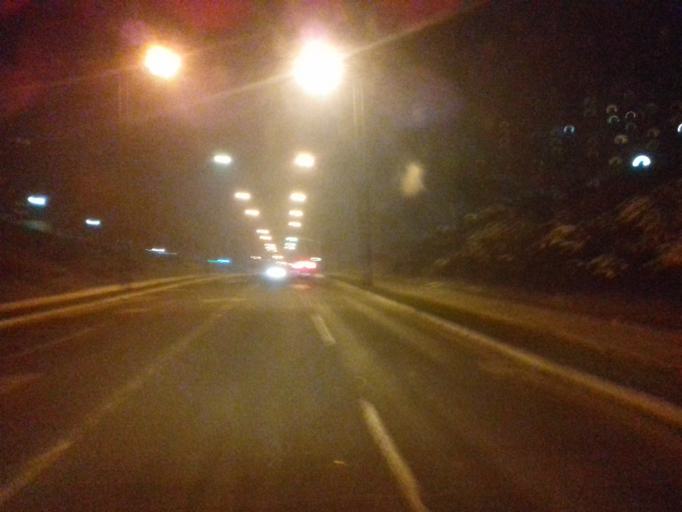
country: BA
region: Federation of Bosnia and Herzegovina
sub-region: Kanton Sarajevo
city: Sarajevo
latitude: 43.8434
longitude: 18.3481
